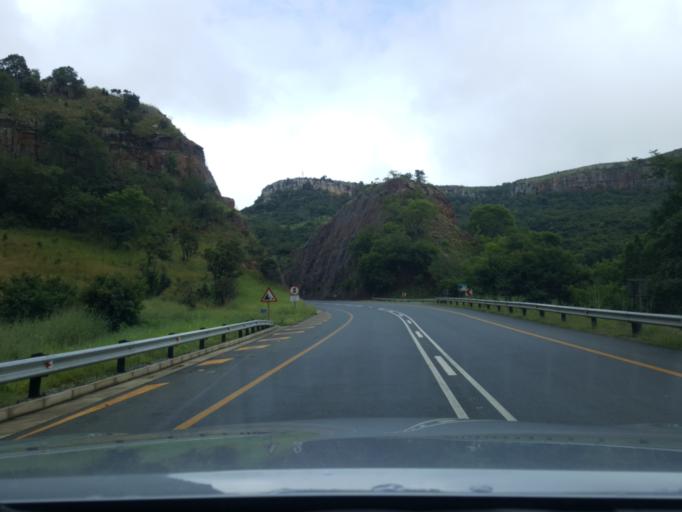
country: ZA
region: Mpumalanga
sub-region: Nkangala District Municipality
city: Belfast
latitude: -25.6463
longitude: 30.3591
